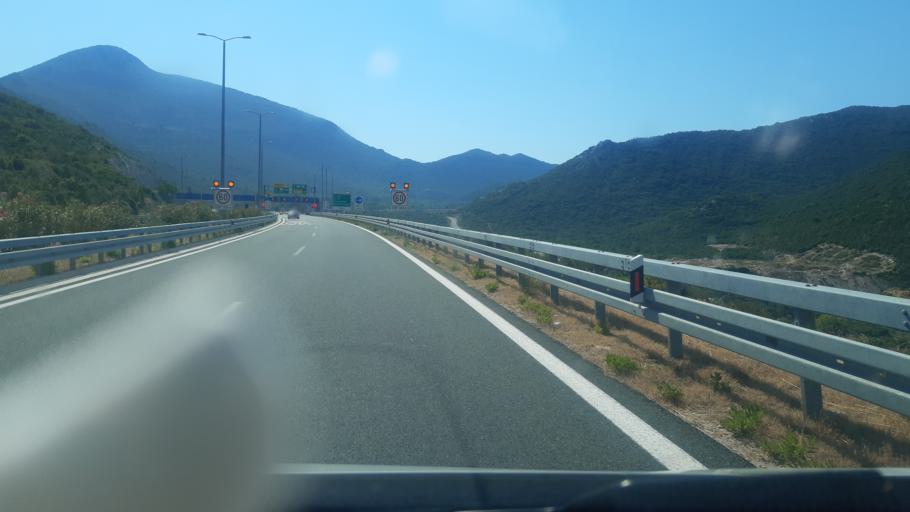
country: HR
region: Dubrovacko-Neretvanska
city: Komin
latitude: 43.1033
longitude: 17.4819
